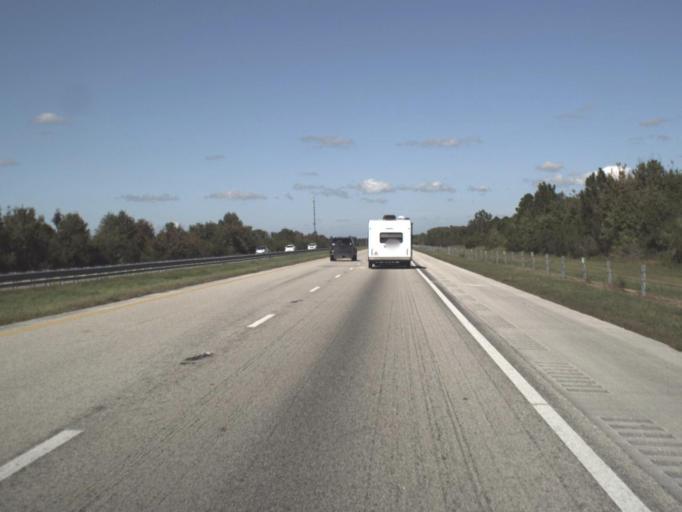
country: US
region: Florida
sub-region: Osceola County
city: Saint Cloud
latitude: 28.0161
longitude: -81.1743
